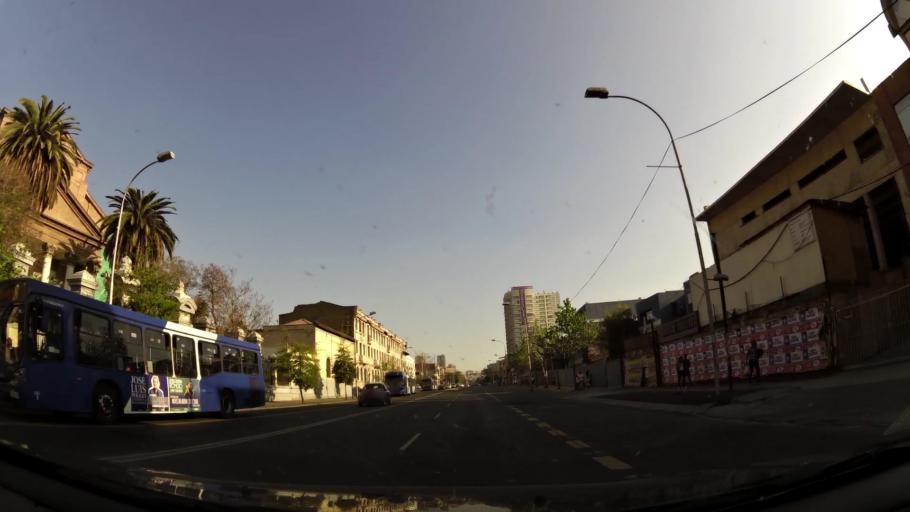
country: CL
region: Santiago Metropolitan
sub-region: Provincia de Santiago
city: Santiago
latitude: -33.4236
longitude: -70.6453
